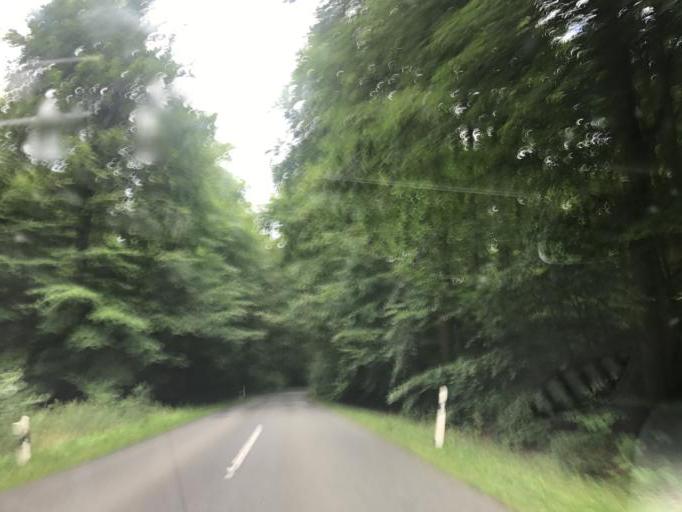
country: DE
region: Mecklenburg-Vorpommern
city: Rechlin
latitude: 53.2377
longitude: 12.6987
